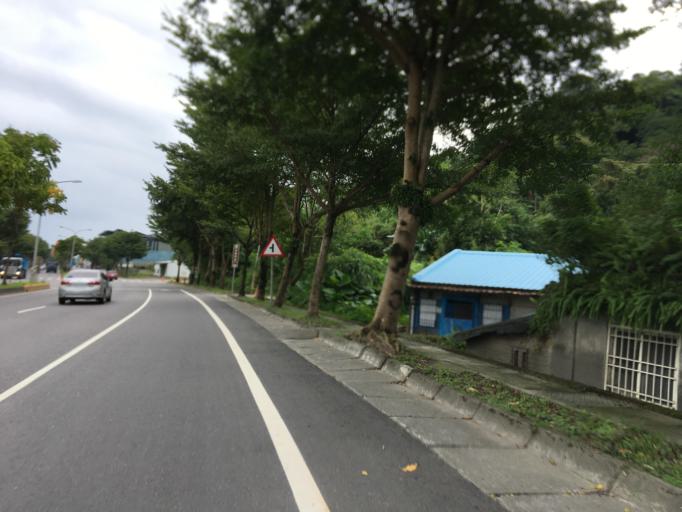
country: TW
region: Taiwan
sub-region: Yilan
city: Yilan
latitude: 24.6147
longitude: 121.8145
